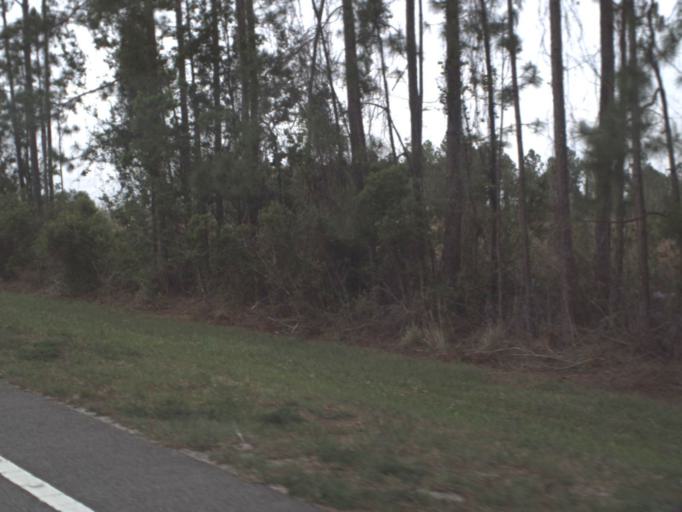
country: US
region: Florida
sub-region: Putnam County
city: Crescent City
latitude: 29.5258
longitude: -81.5106
